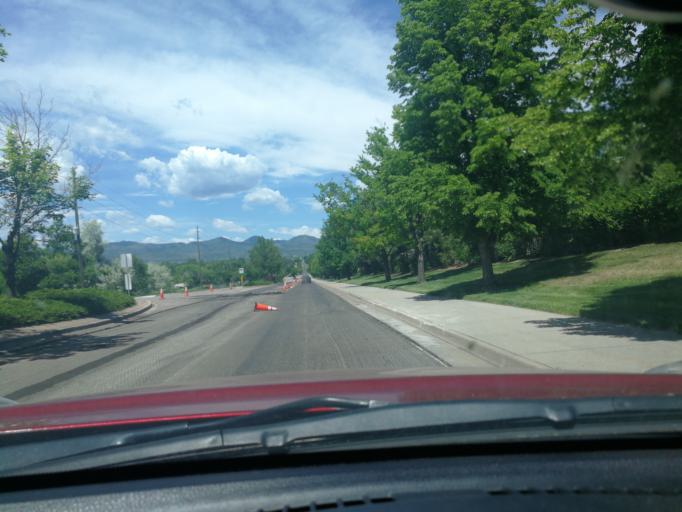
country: US
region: Colorado
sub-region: Jefferson County
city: Columbine
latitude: 39.6099
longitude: -105.0599
